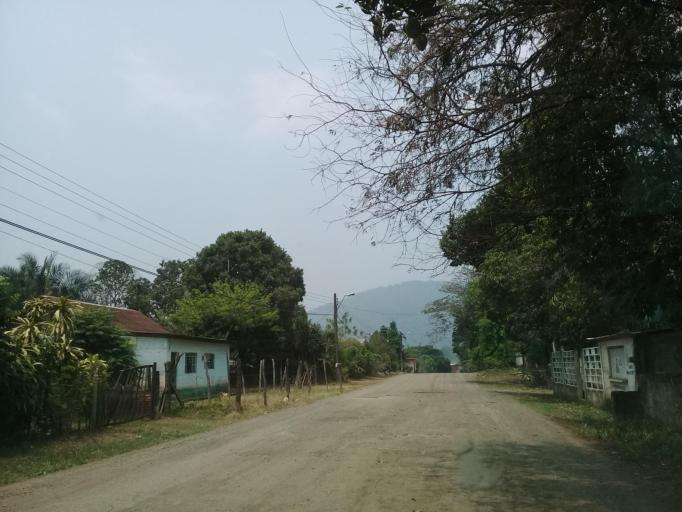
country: MX
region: Veracruz
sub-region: Tezonapa
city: Laguna Chica (Pueblo Nuevo)
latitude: 18.5463
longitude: -96.7331
